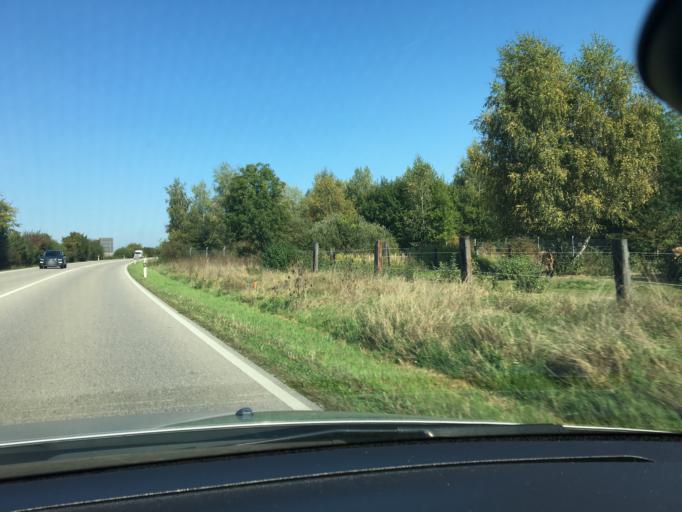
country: DE
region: Bavaria
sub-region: Upper Bavaria
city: Stammham
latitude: 48.3090
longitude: 11.8784
